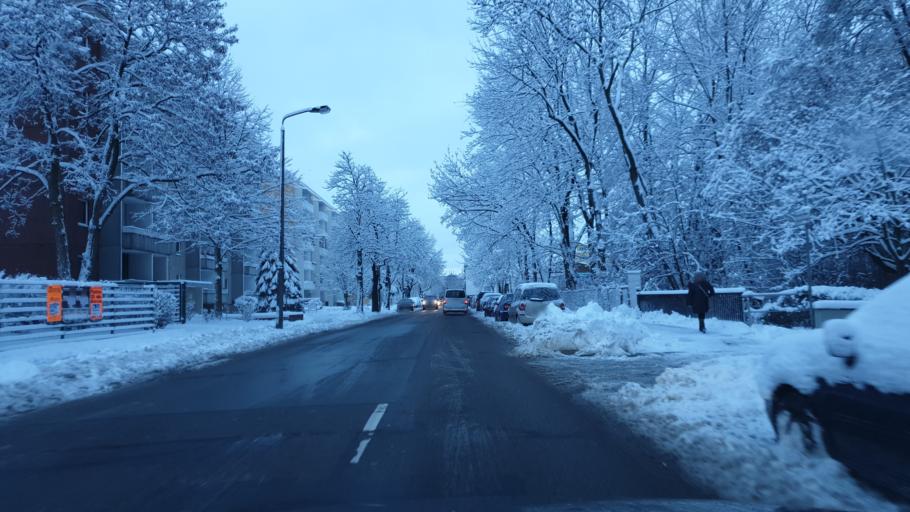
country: DE
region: Saxony
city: Chemnitz
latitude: 50.8446
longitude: 12.9193
